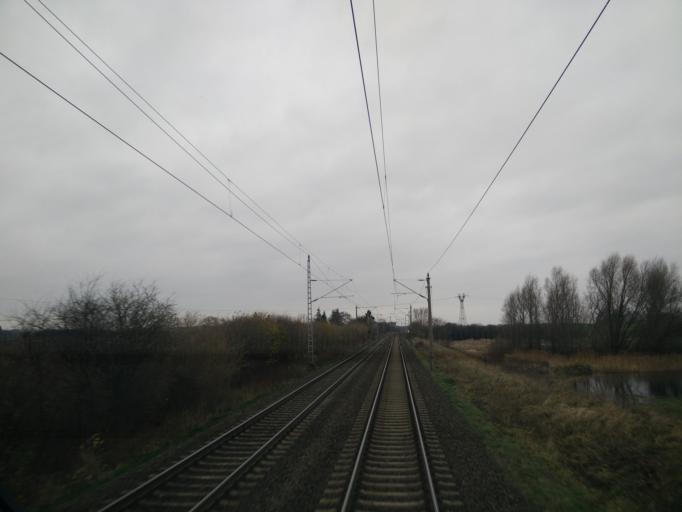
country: DE
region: Mecklenburg-Vorpommern
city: Seehof
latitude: 53.6788
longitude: 11.4070
